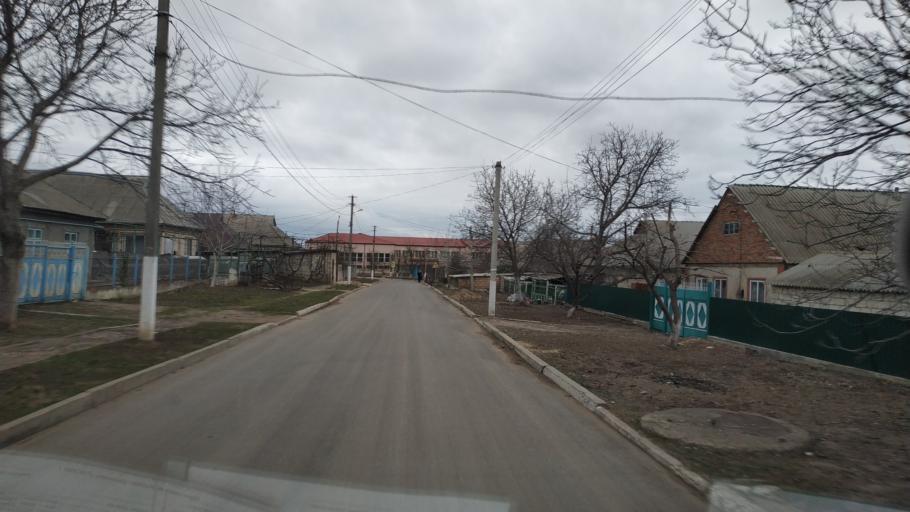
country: MD
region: Bender
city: Bender
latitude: 46.7771
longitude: 29.4801
